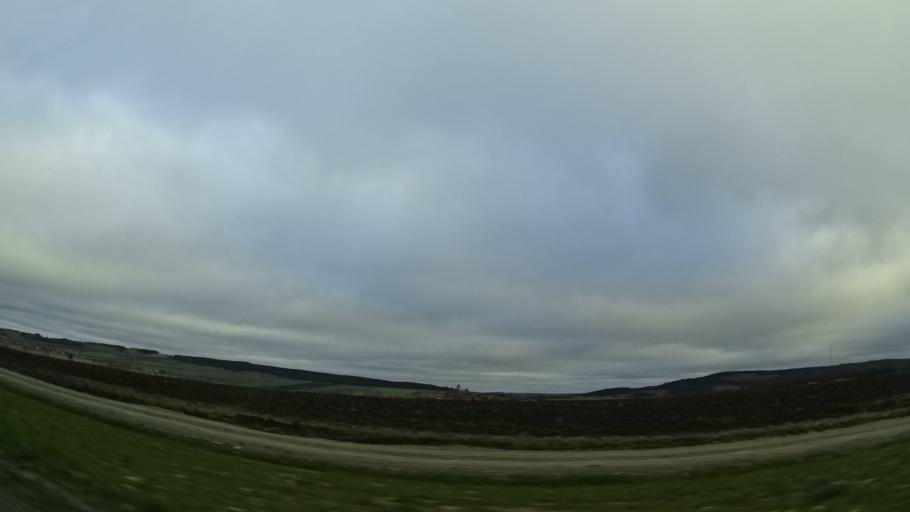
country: DE
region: Thuringia
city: Rottenbach
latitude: 50.7403
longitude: 11.1535
